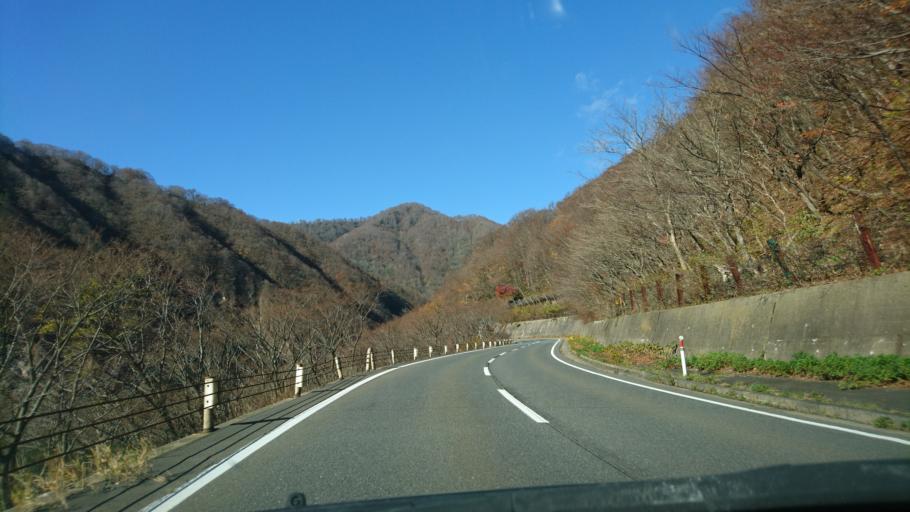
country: JP
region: Iwate
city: Kitakami
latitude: 39.3010
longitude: 140.8964
